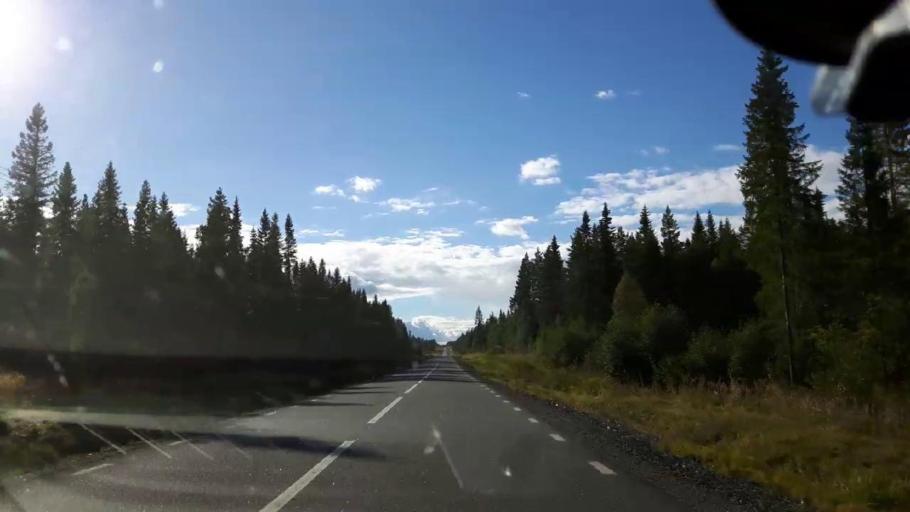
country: SE
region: Jaemtland
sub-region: Stroemsunds Kommun
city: Stroemsund
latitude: 63.5404
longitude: 15.9761
